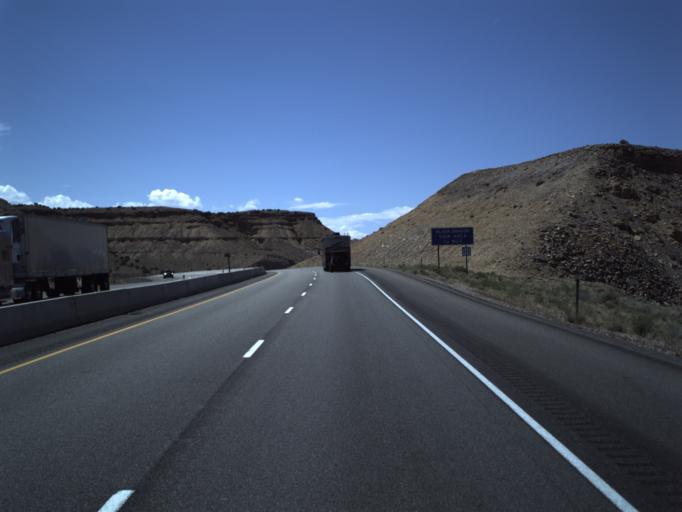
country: US
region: Utah
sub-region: Carbon County
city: East Carbon City
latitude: 38.9376
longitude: -110.4711
